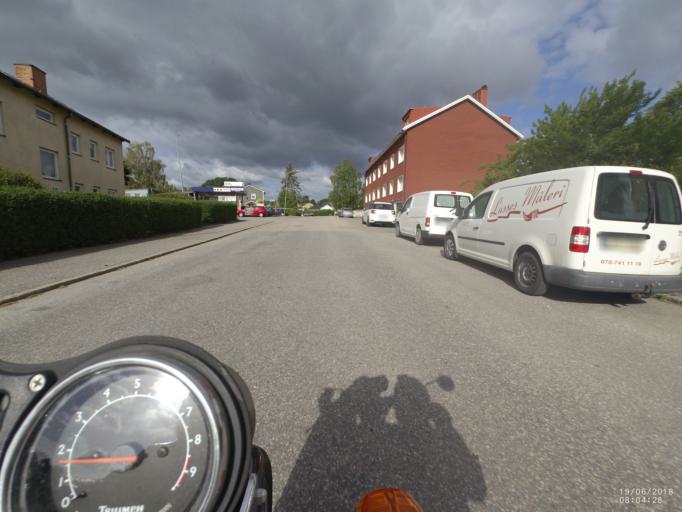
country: SE
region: Soedermanland
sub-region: Nykopings Kommun
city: Nykoping
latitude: 58.7727
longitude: 16.9830
